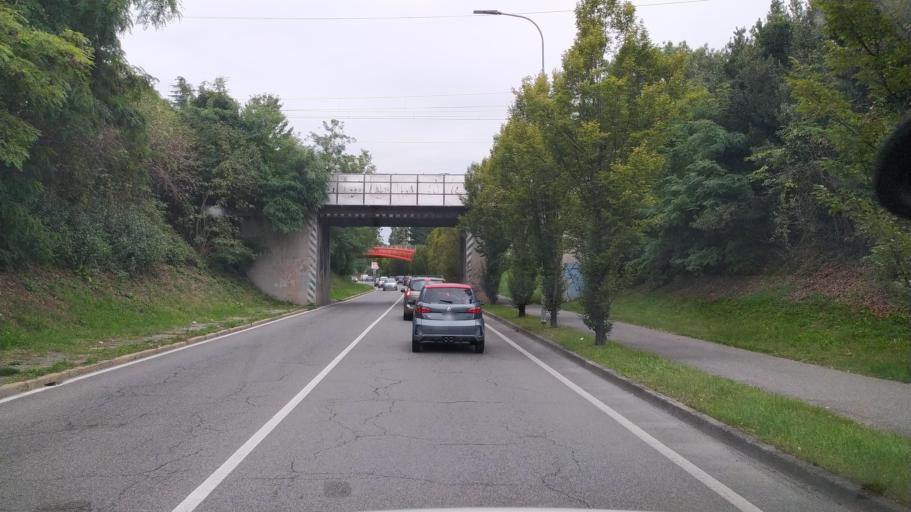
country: IT
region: Lombardy
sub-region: Provincia di Monza e Brianza
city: Seregno
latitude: 45.6426
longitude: 9.2079
